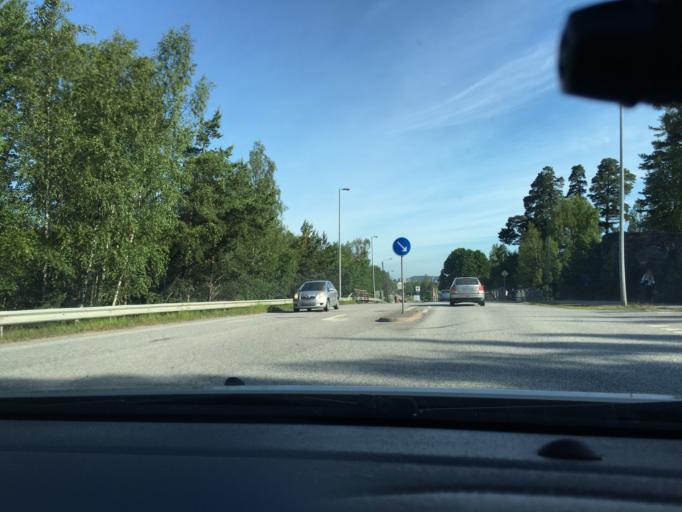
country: SE
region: Stockholm
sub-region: Sodertalje Kommun
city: Pershagen
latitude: 59.1623
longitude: 17.6419
